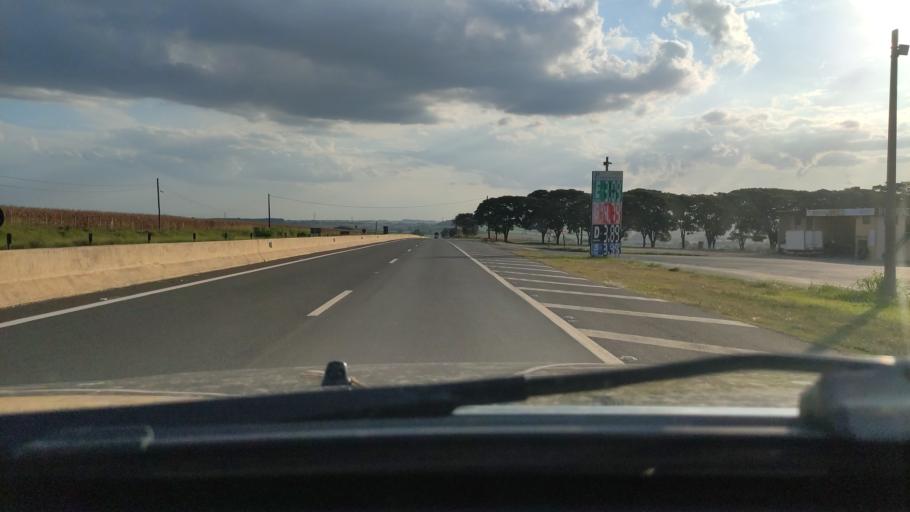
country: BR
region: Sao Paulo
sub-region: Artur Nogueira
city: Artur Nogueira
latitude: -22.4700
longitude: -47.1168
